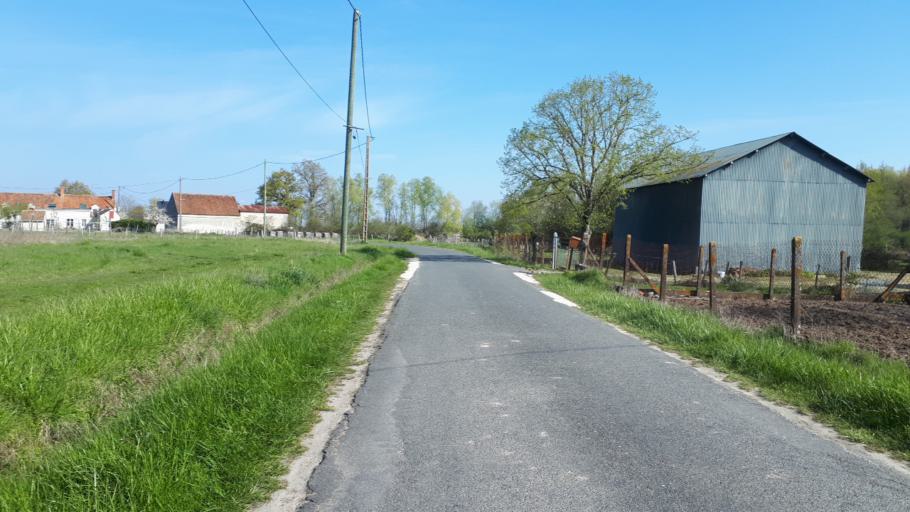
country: FR
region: Centre
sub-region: Departement du Loir-et-Cher
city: Contres
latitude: 47.3794
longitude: 1.3937
